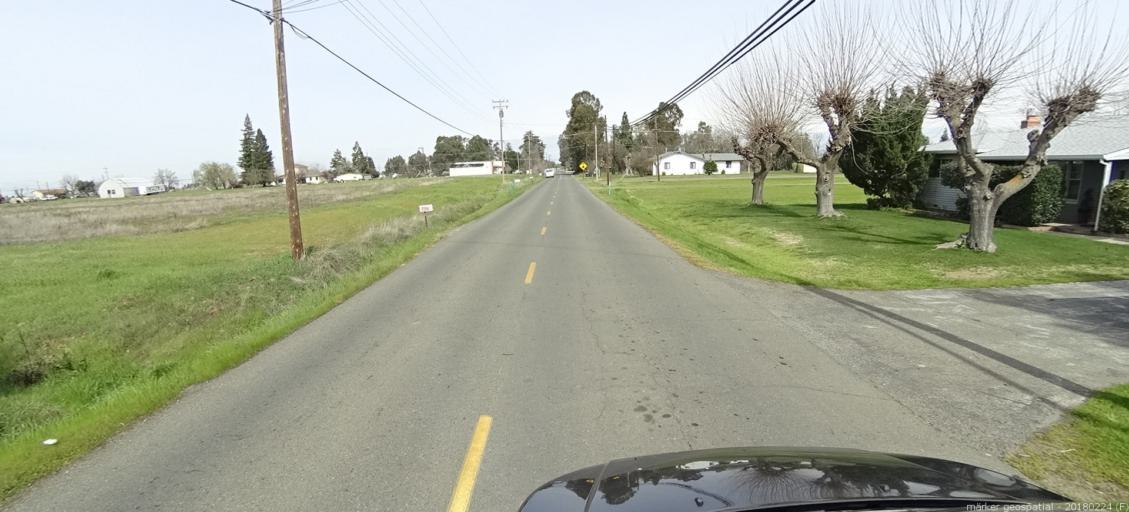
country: US
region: California
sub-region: Sacramento County
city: Elverta
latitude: 38.7122
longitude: -121.4666
